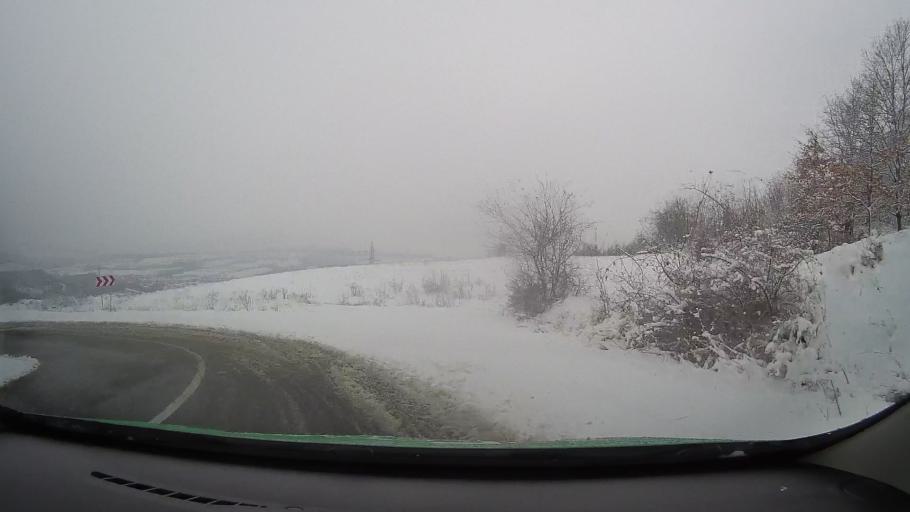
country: RO
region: Hunedoara
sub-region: Comuna Unirea
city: Unirea
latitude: 45.6593
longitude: 22.9087
